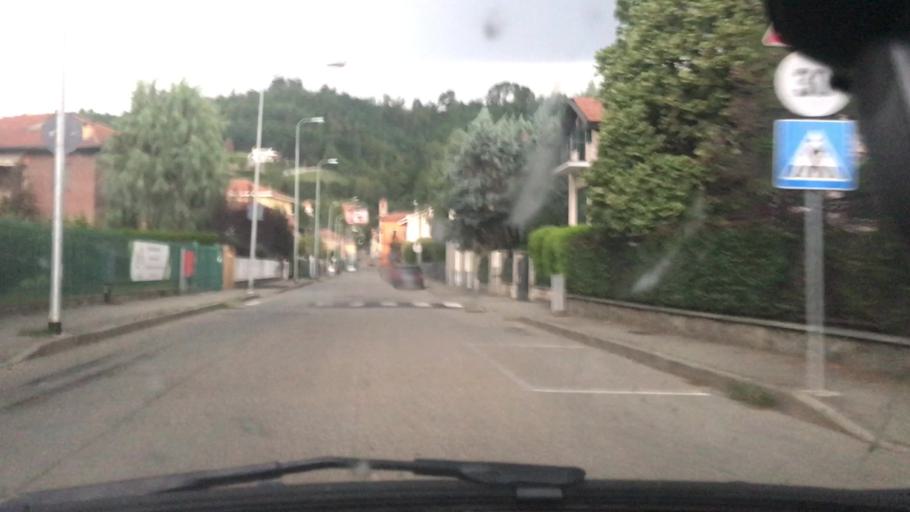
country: IT
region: Piedmont
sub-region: Provincia di Biella
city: Ronco Biellese
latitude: 45.5725
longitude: 8.0761
